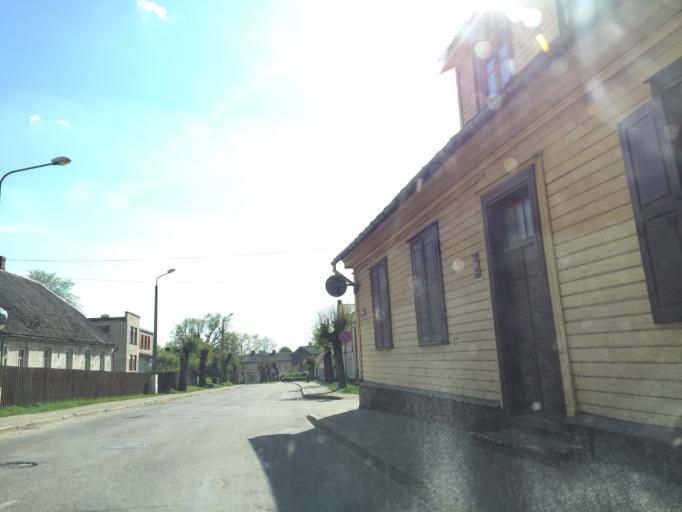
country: LV
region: Limbazu Rajons
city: Limbazi
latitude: 57.5126
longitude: 24.7087
